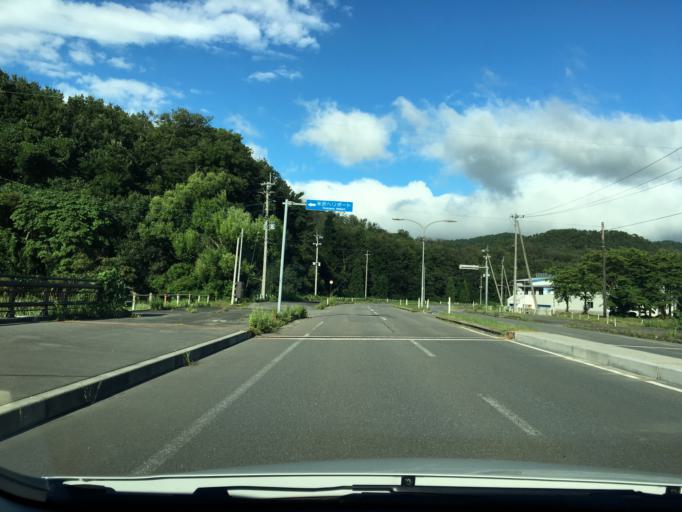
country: JP
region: Yamagata
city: Yonezawa
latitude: 37.9117
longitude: 140.1665
